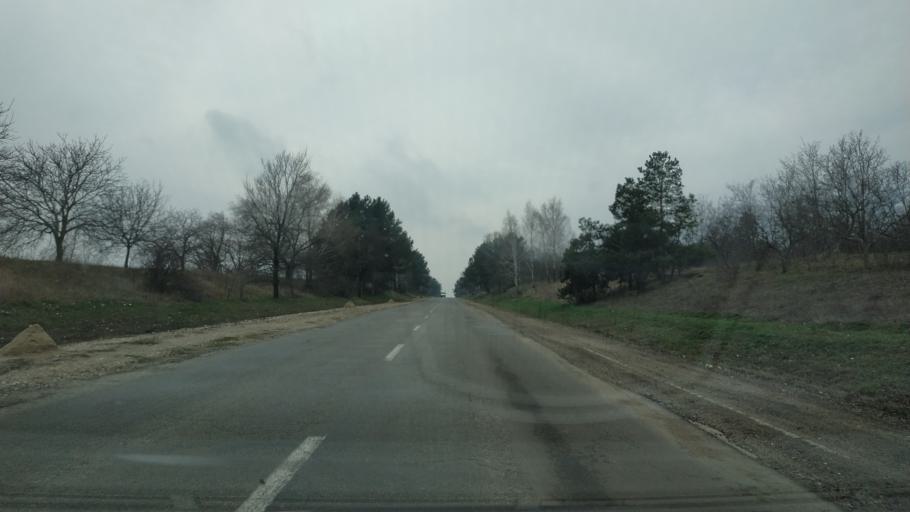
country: MD
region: Cahul
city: Cahul
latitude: 45.9415
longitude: 28.2937
